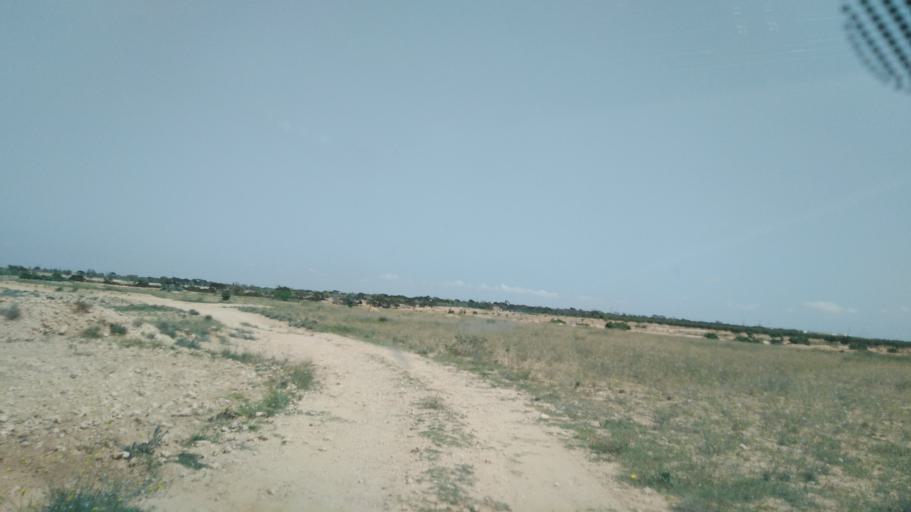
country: TN
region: Safaqis
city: Sfax
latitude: 34.7197
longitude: 10.5657
